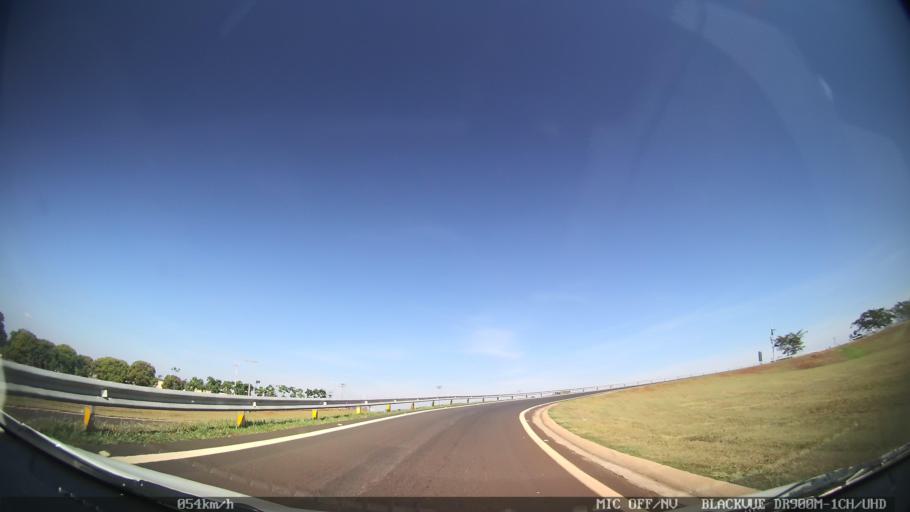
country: BR
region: Sao Paulo
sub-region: Jardinopolis
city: Jardinopolis
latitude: -21.0926
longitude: -47.7924
